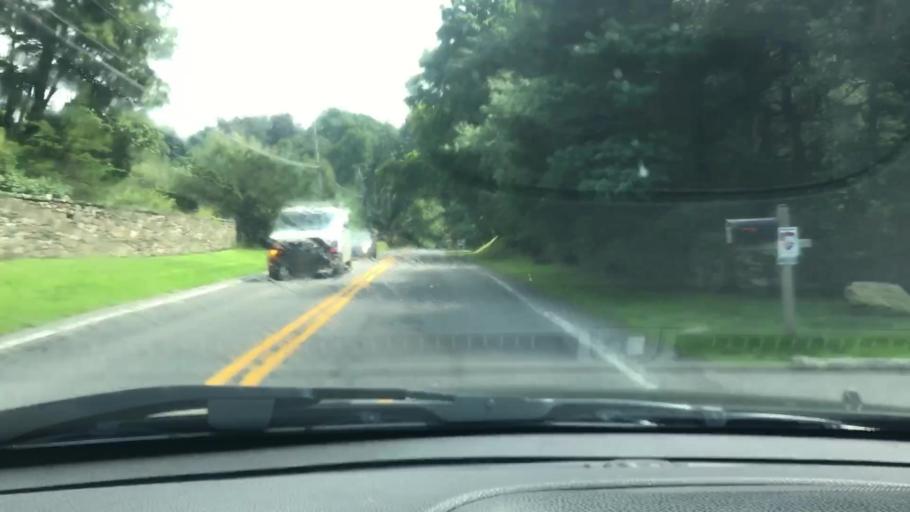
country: US
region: New York
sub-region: Westchester County
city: Bedford
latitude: 41.1830
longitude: -73.6144
